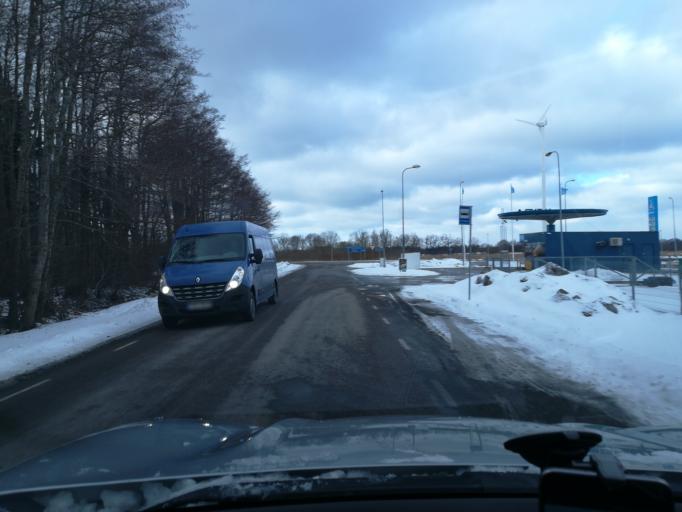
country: EE
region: Harju
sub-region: Keila linn
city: Keila
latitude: 59.4452
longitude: 24.3814
